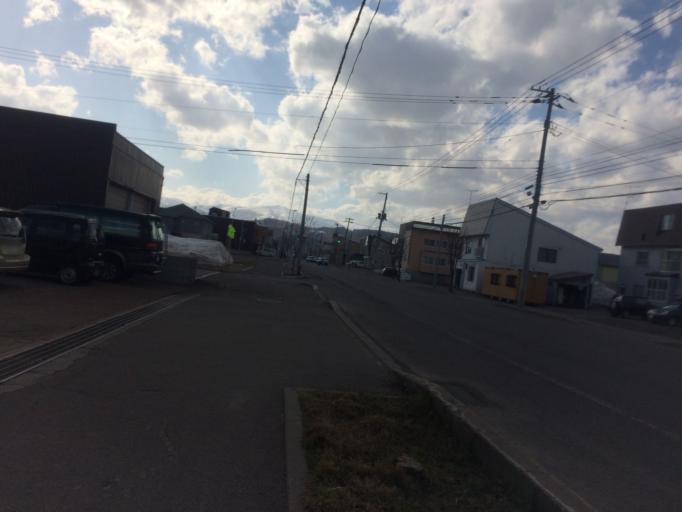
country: JP
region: Hokkaido
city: Niseko Town
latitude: 42.9036
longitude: 140.7613
